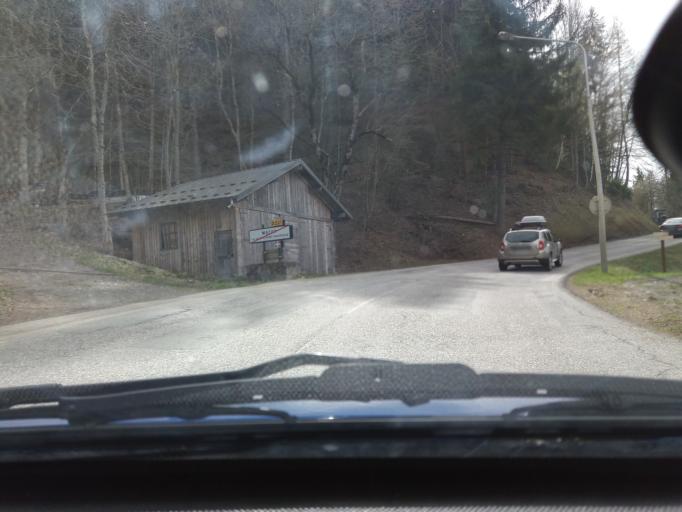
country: FR
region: Rhone-Alpes
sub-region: Departement de la Savoie
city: Macot-la-Plagne
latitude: 45.5509
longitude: 6.6748
